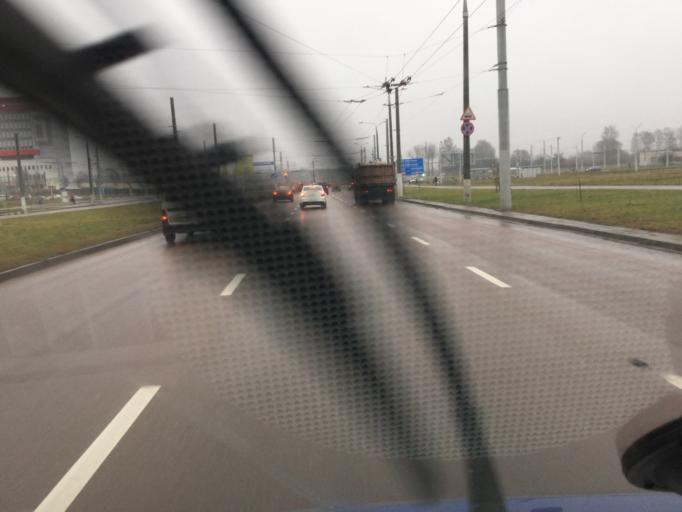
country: BY
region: Vitebsk
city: Vitebsk
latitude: 55.1586
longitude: 30.2310
